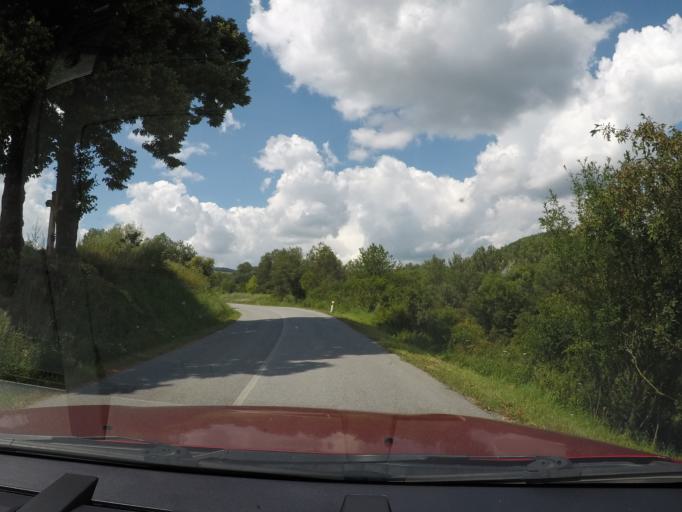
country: SK
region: Kosicky
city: Gelnica
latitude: 48.9216
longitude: 21.0660
